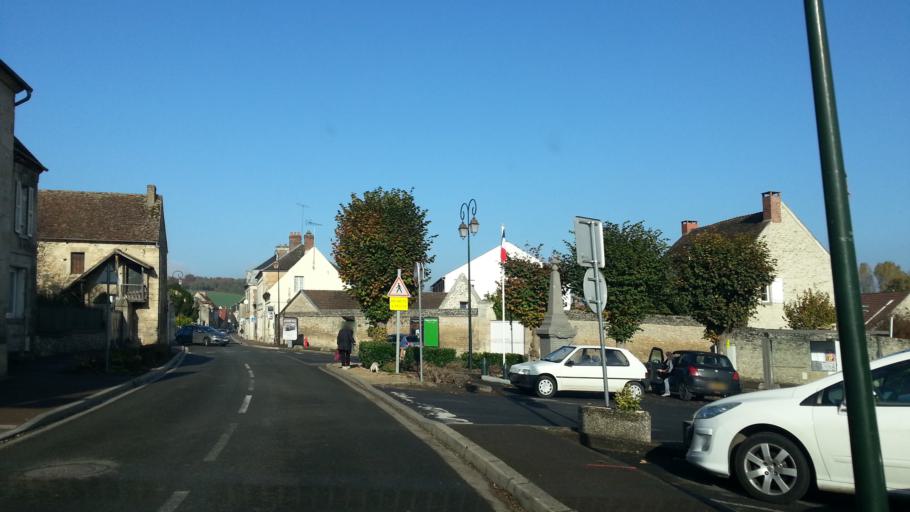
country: FR
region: Picardie
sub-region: Departement de l'Oise
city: Balagny-sur-Therain
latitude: 49.2957
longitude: 2.3362
